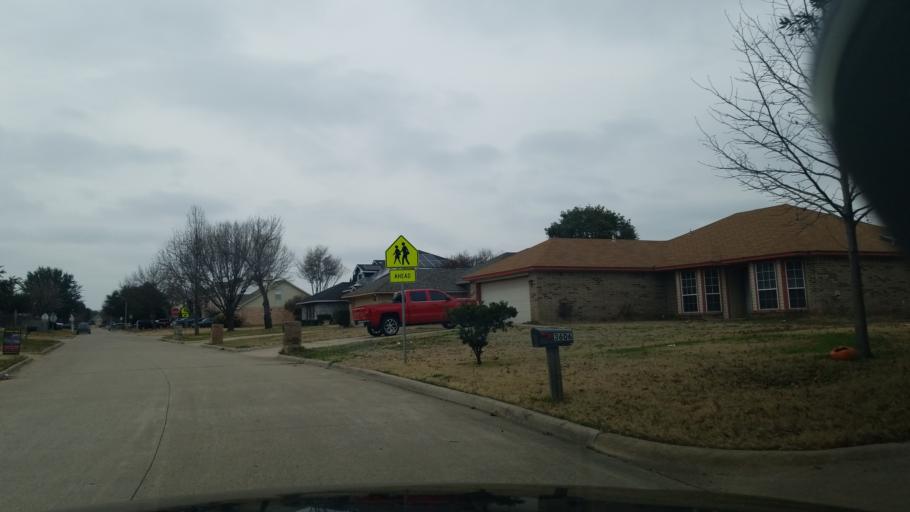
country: US
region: Texas
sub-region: Denton County
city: Hickory Creek
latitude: 33.1365
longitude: -97.0488
